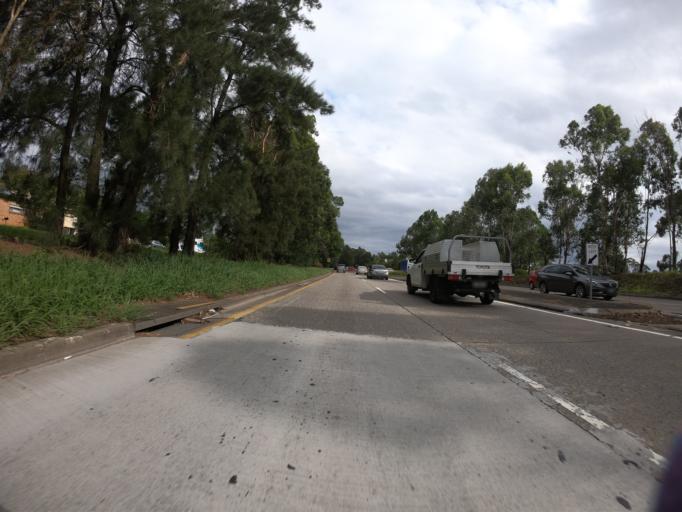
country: AU
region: New South Wales
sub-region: Parramatta
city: Northmead
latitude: -33.7701
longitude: 150.9594
